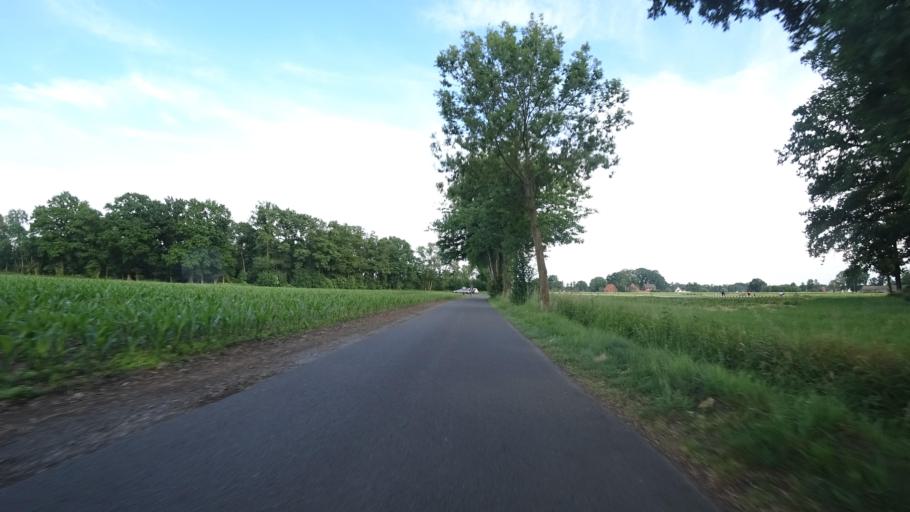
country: DE
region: North Rhine-Westphalia
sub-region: Regierungsbezirk Detmold
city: Guetersloh
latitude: 51.9114
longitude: 8.4452
